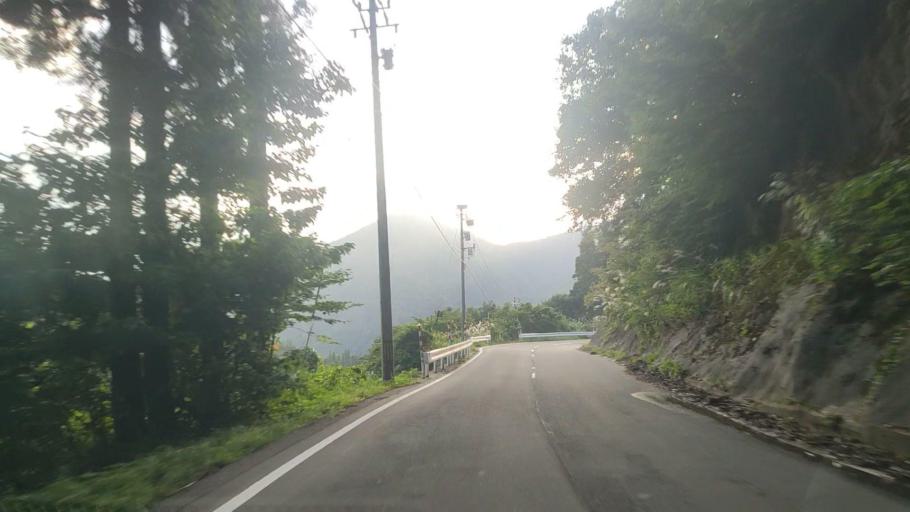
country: JP
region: Toyama
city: Yatsuomachi-higashikumisaka
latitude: 36.4796
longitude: 137.0318
